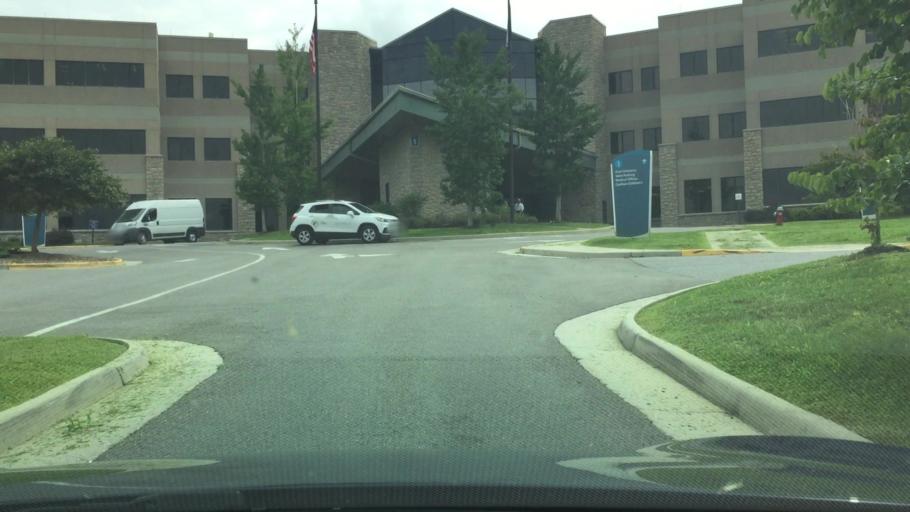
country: US
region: Virginia
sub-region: City of Radford
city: Radford
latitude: 37.0891
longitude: -80.5064
